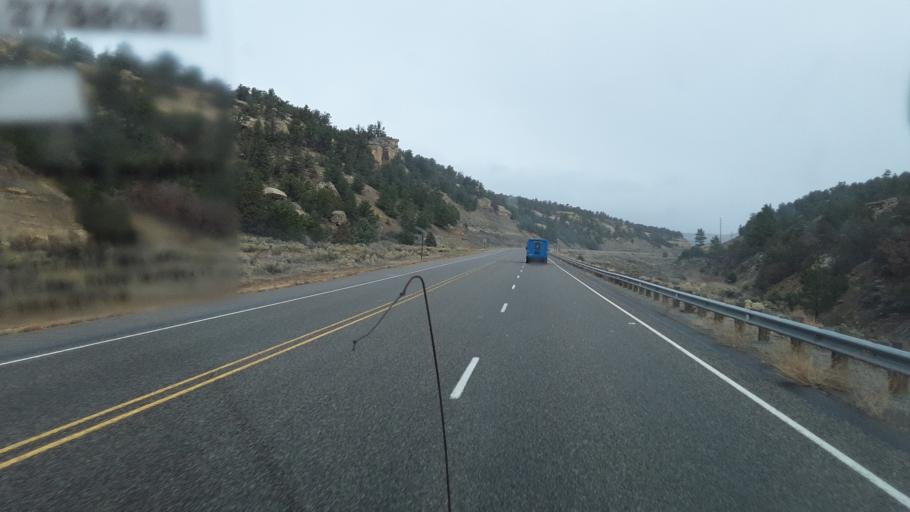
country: US
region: New Mexico
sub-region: Rio Arriba County
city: Tierra Amarilla
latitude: 36.4263
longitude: -106.4788
